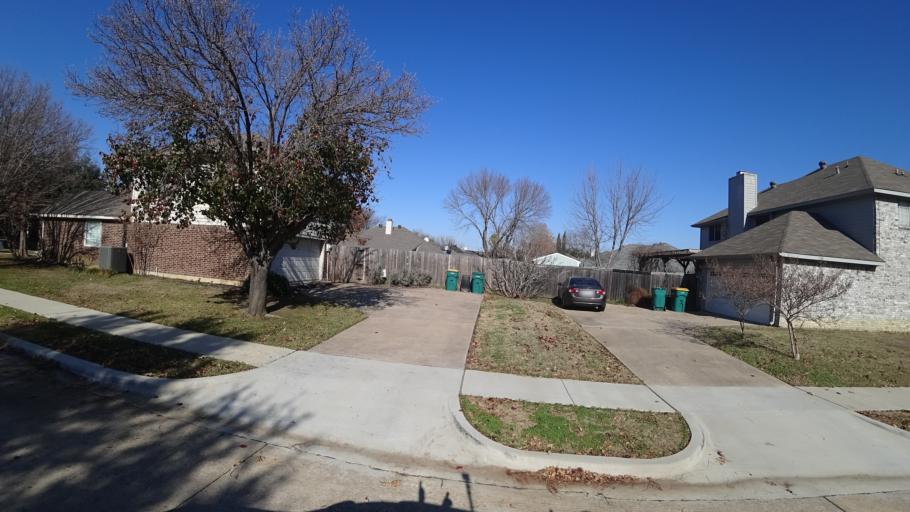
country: US
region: Texas
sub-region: Denton County
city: Lewisville
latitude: 33.0100
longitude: -97.0172
